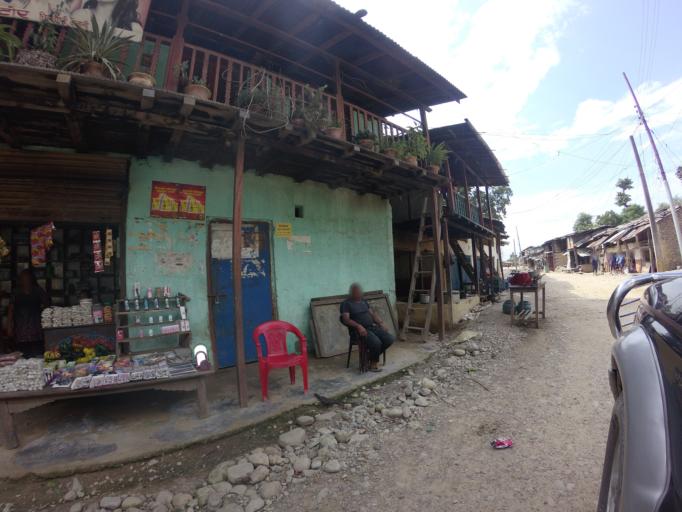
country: NP
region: Far Western
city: Tikapur
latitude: 28.6474
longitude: 81.2846
